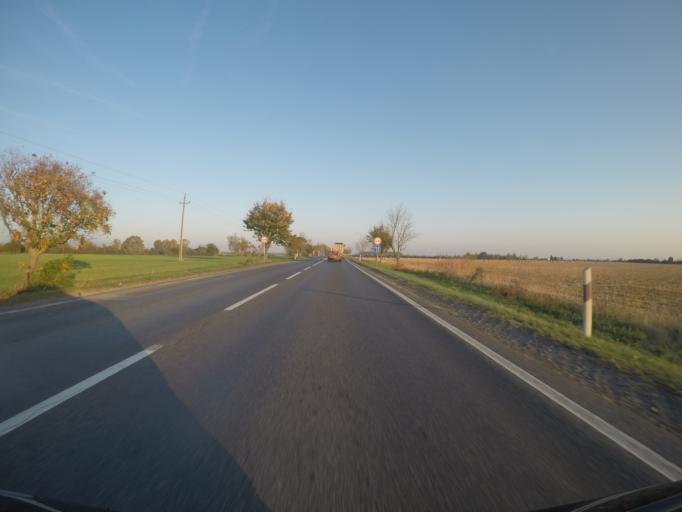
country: HU
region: Baranya
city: Szentlorinc
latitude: 46.0414
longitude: 17.9233
